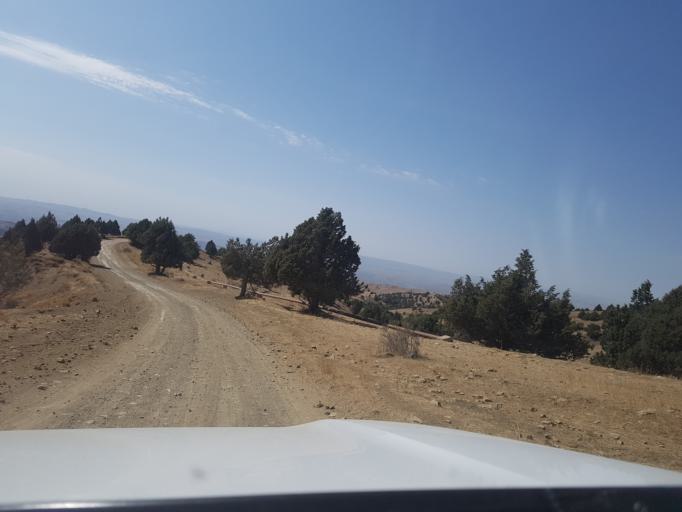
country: TM
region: Ahal
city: Baharly
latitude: 38.3184
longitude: 56.9545
